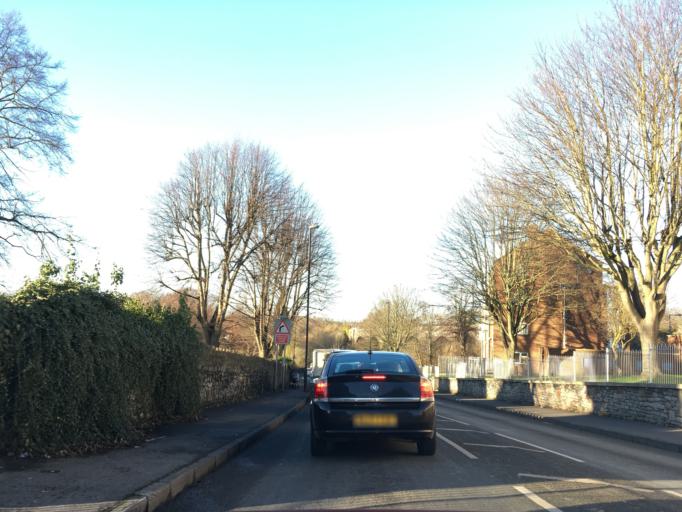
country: GB
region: England
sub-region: South Gloucestershire
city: Kingswood
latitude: 51.4698
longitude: -2.5506
